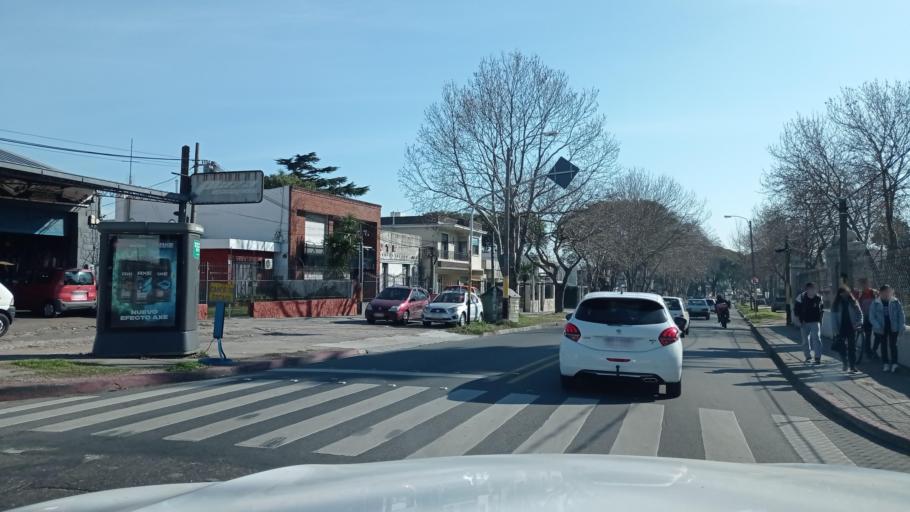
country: UY
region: Montevideo
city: Montevideo
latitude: -34.8632
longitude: -56.1810
